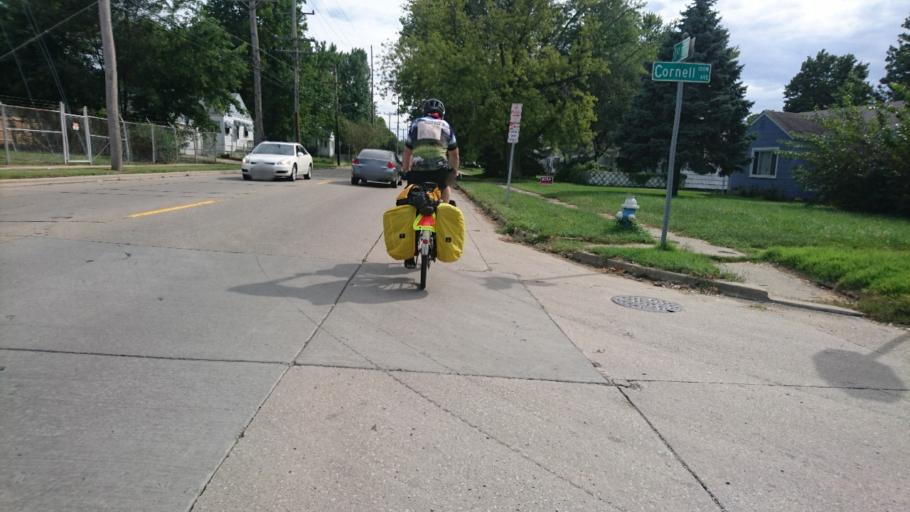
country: US
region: Illinois
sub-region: Sangamon County
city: Southern View
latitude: 39.7775
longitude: -89.6543
